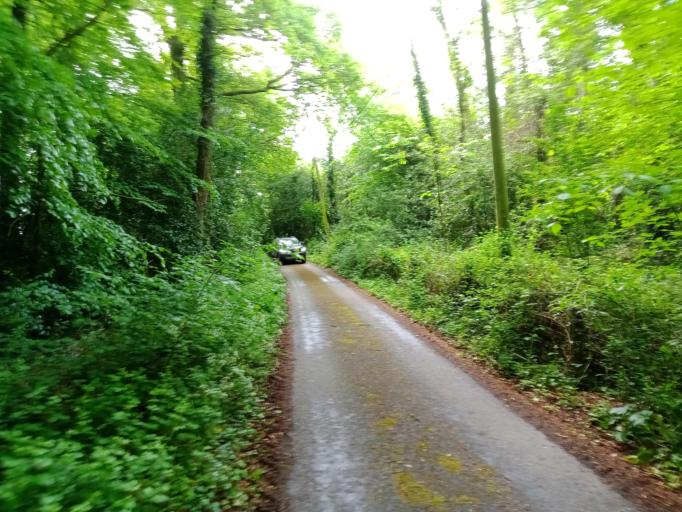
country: IE
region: Leinster
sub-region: Kilkenny
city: Thomastown
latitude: 52.5072
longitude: -7.1304
